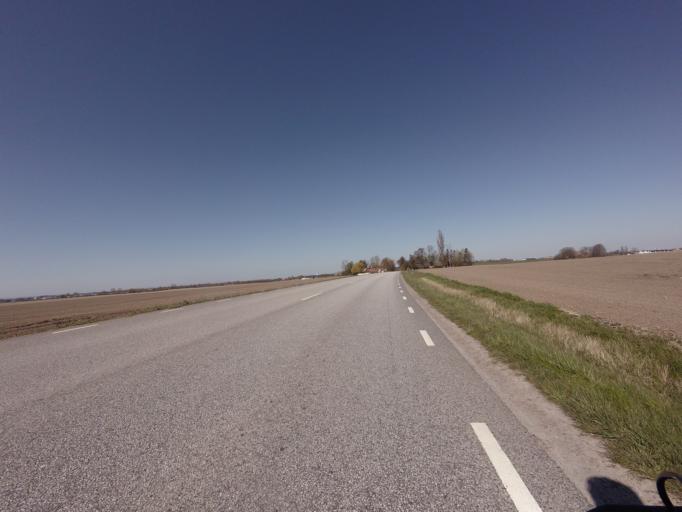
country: SE
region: Skane
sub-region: Vellinge Kommun
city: Vellinge
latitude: 55.4671
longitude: 13.0565
